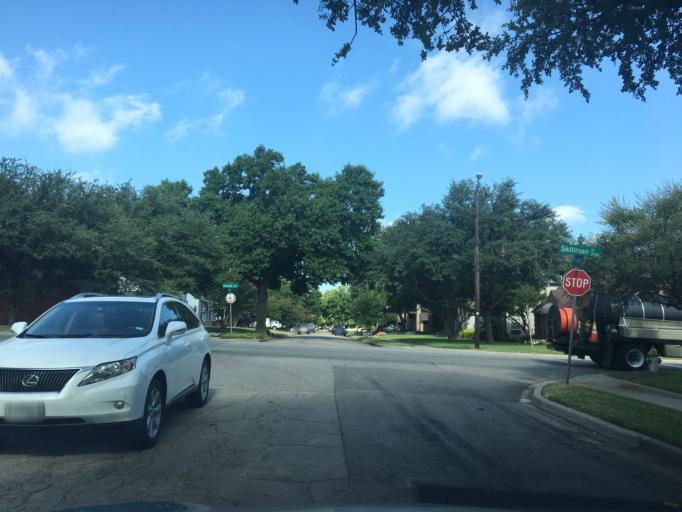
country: US
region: Texas
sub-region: Dallas County
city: Highland Park
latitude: 32.8324
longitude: -96.7603
